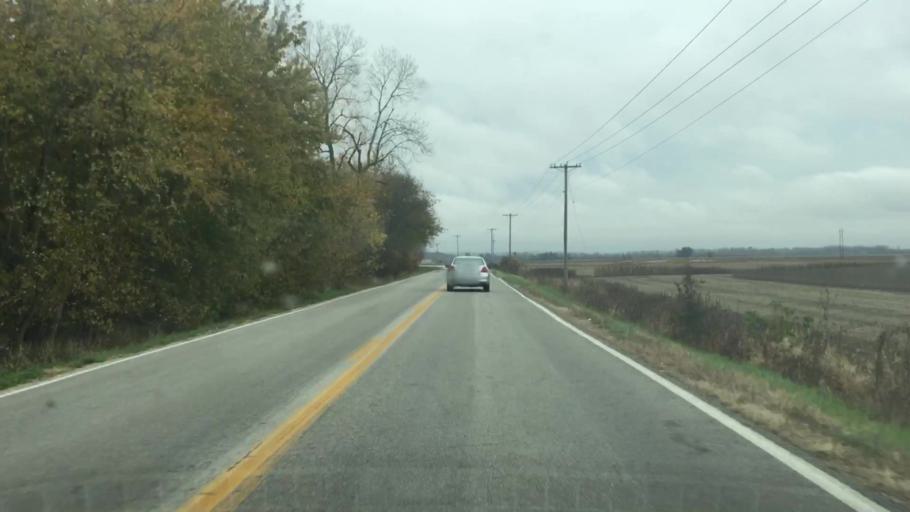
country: US
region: Missouri
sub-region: Gasconade County
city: Hermann
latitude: 38.7247
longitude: -91.4868
